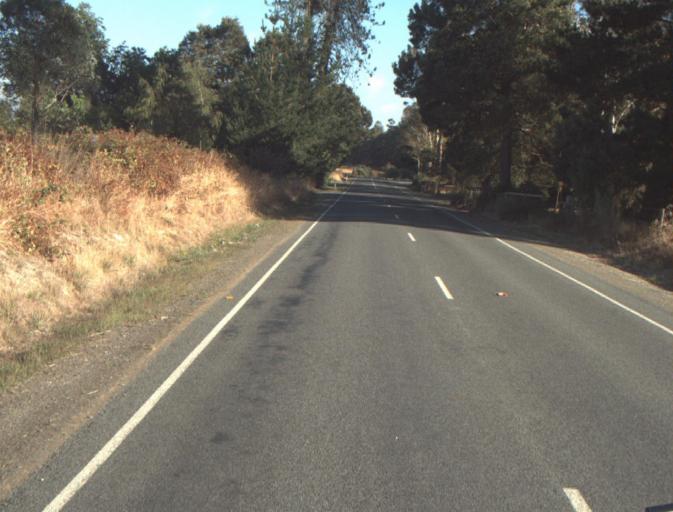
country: AU
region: Tasmania
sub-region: Launceston
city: Mayfield
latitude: -41.2313
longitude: 147.2098
